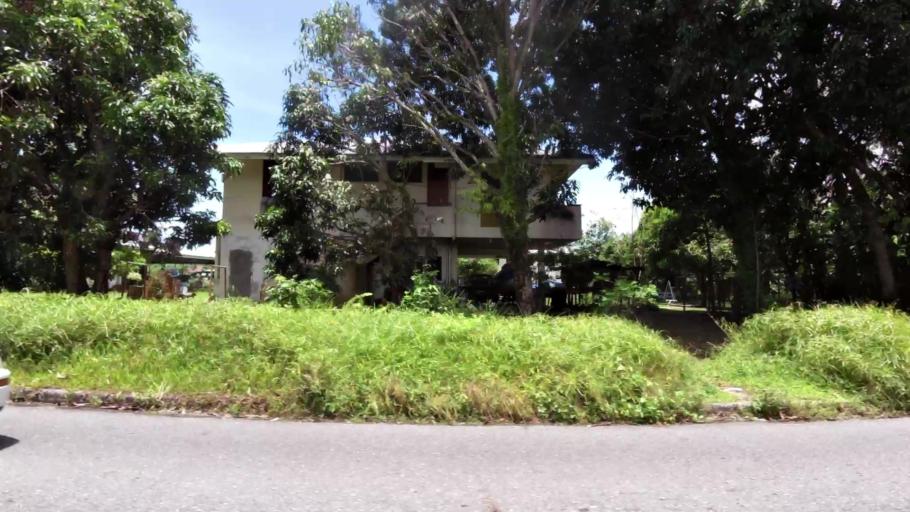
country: BN
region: Belait
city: Kuala Belait
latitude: 4.5854
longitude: 114.2378
